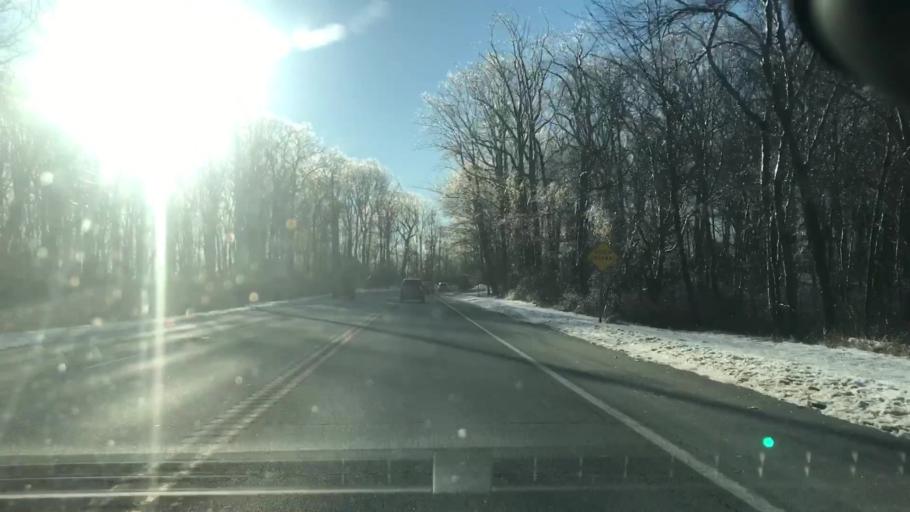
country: US
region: New Jersey
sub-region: Morris County
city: Netcong
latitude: 40.8794
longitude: -74.6937
